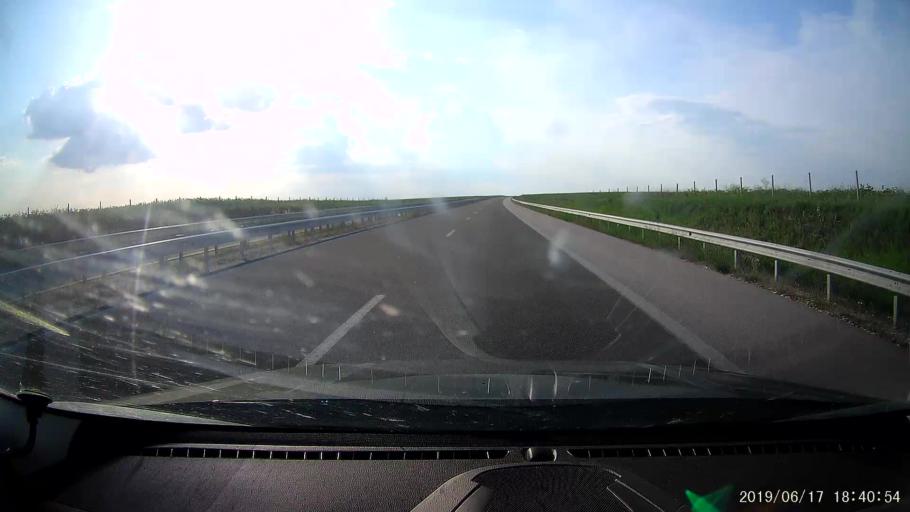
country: BG
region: Stara Zagora
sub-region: Obshtina Chirpan
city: Chirpan
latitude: 42.1624
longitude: 25.2665
